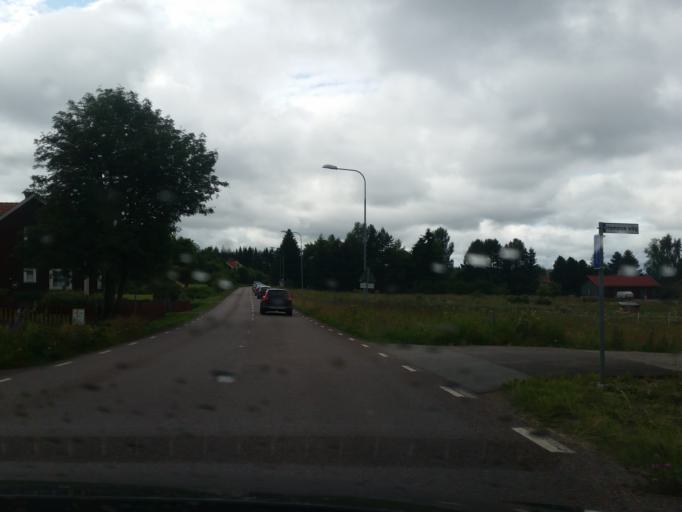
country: SE
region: Dalarna
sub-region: Leksand Municipality
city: Leksand
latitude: 60.7176
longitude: 14.9678
